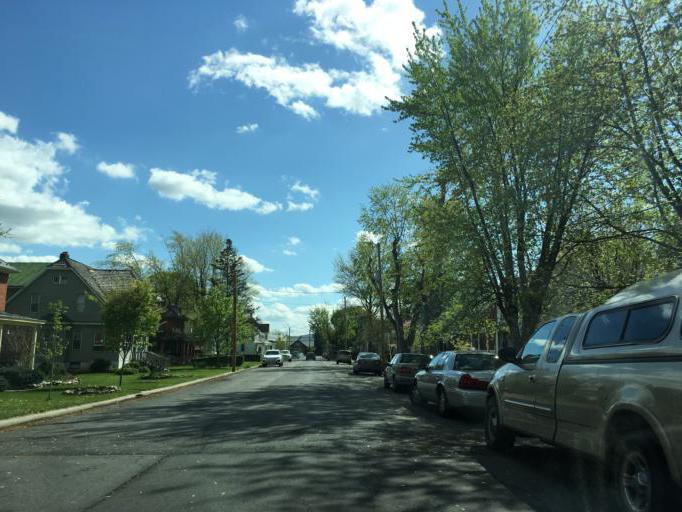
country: US
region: Maryland
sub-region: Frederick County
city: Thurmont
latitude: 39.6241
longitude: -77.4049
